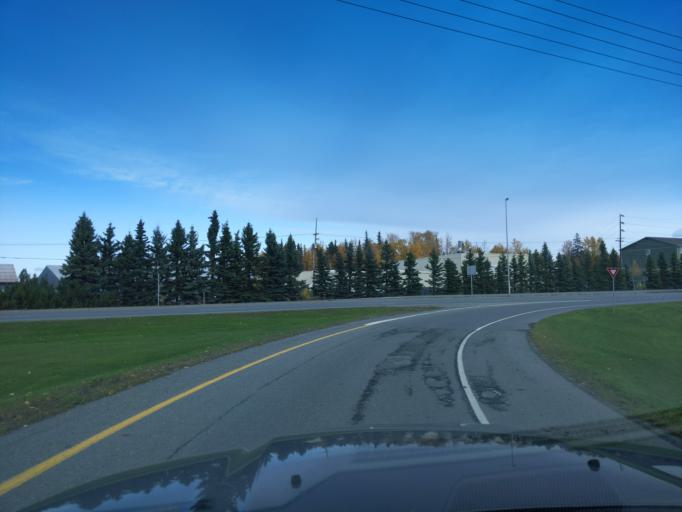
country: US
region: Alaska
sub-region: Anchorage Municipality
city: Anchorage
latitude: 61.1734
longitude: -149.9420
